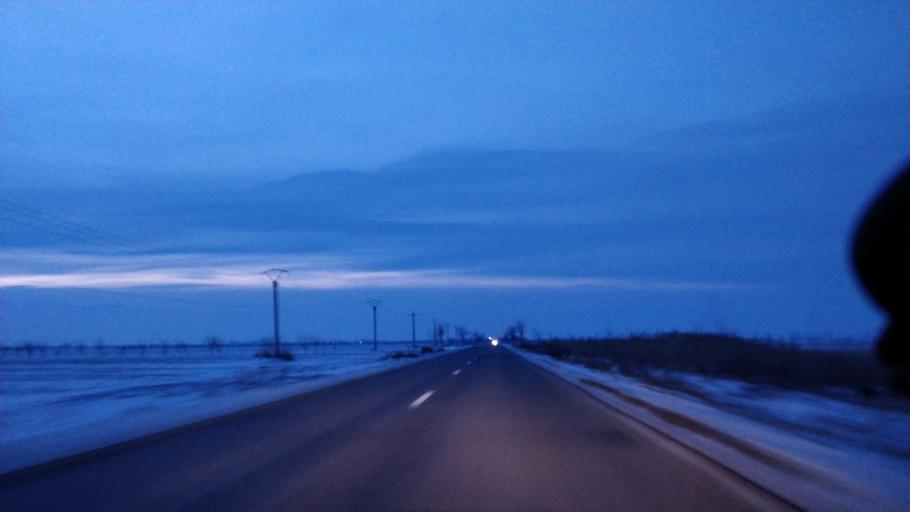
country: RO
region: Vrancea
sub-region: Comuna Vulturu
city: Vadu Rosca
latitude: 45.6021
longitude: 27.4562
